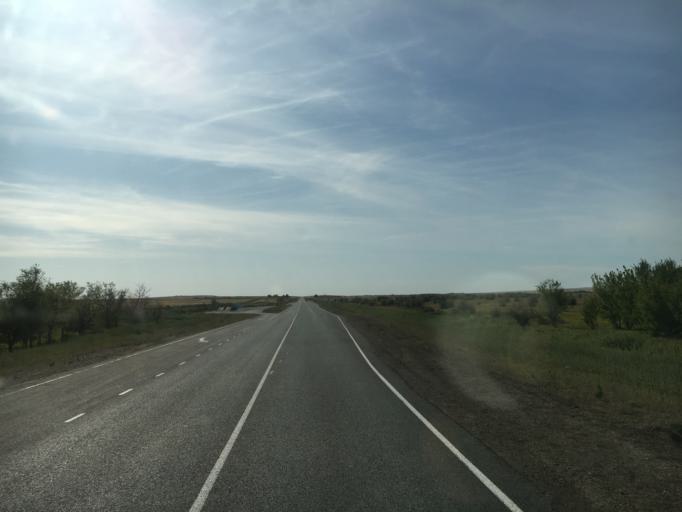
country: KZ
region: Batys Qazaqstan
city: Kamenka
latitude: 51.1074
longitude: 50.4165
